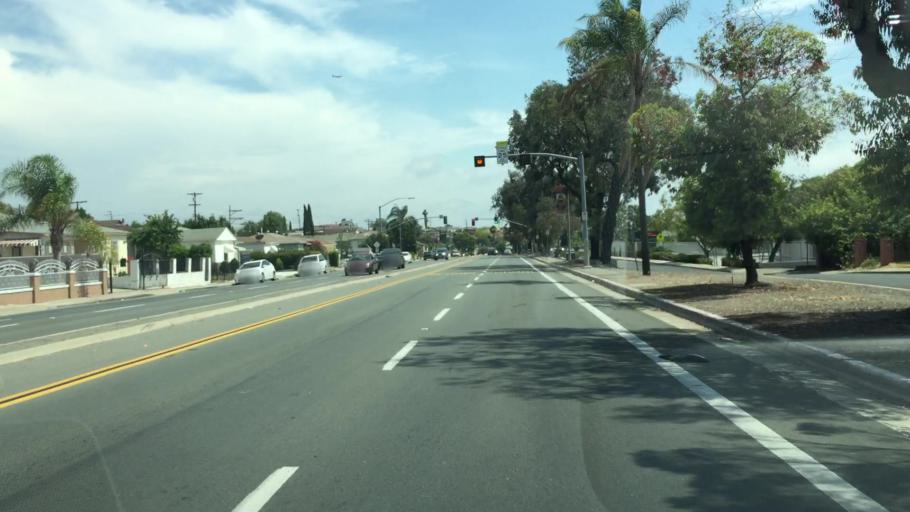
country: US
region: California
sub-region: San Diego County
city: Lemon Grove
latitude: 32.7336
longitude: -117.0798
